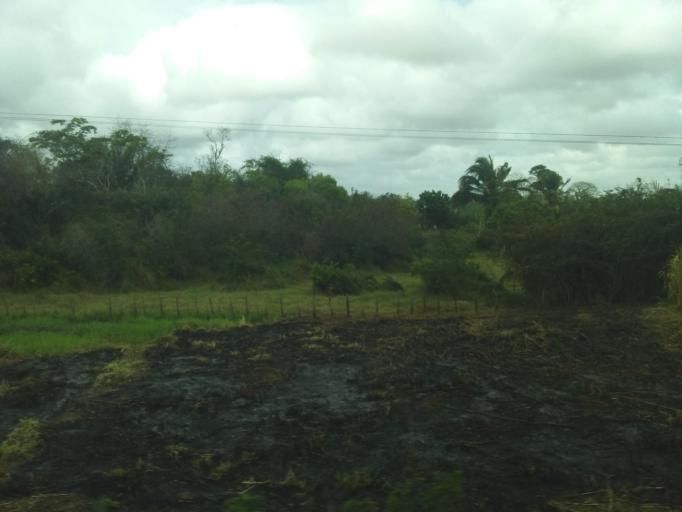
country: BR
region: Maranhao
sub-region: Itapecuru Mirim
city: Itapecuru Mirim
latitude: -3.1083
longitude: -44.3293
